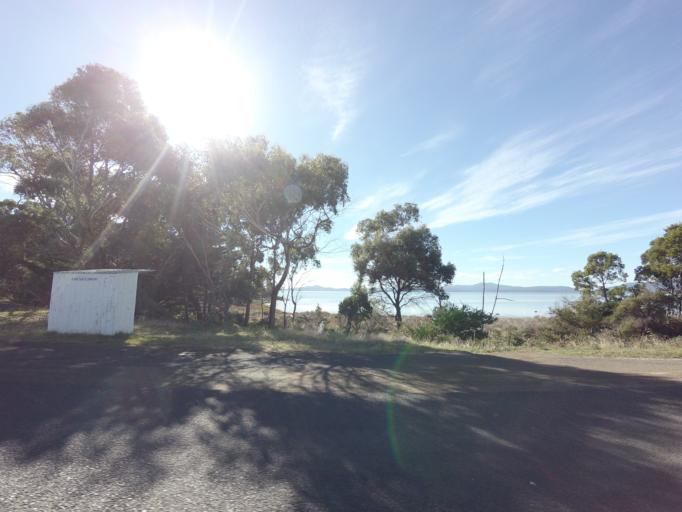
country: AU
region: Tasmania
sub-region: Clarence
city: Sandford
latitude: -43.0071
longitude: 147.7071
